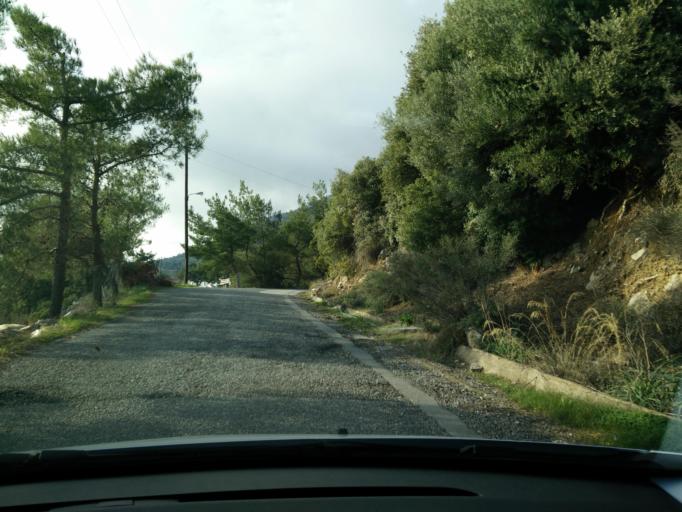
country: GR
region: Crete
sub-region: Nomos Lasithiou
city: Gra Liyia
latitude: 35.0290
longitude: 25.5524
